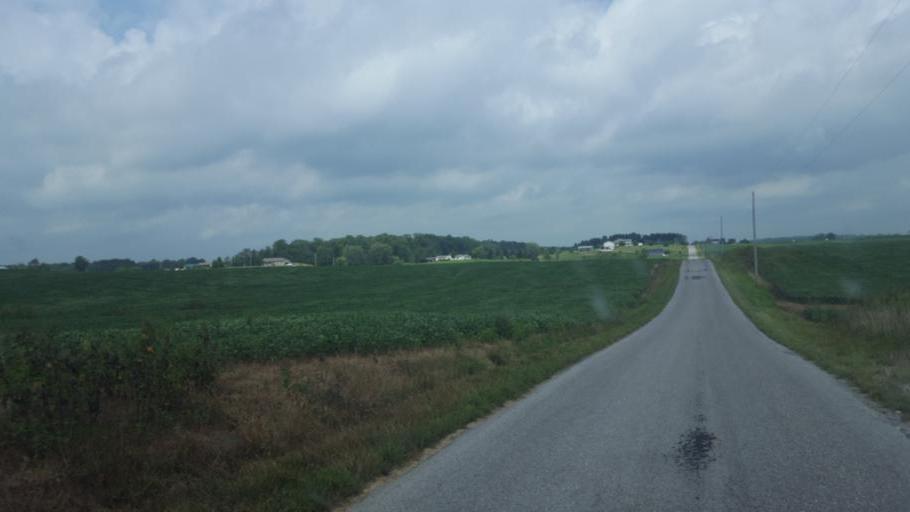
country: US
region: Ohio
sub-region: Morrow County
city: Mount Gilead
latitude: 40.5404
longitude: -82.7205
